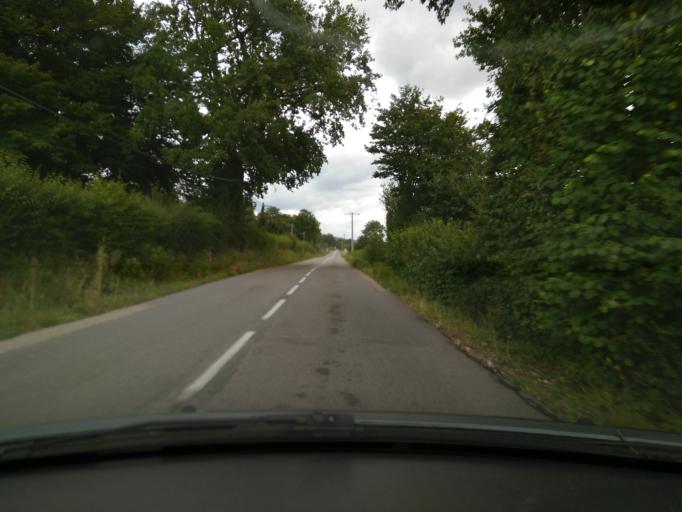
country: FR
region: Rhone-Alpes
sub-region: Departement de l'Isere
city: Chatonnay
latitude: 45.4206
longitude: 5.1642
